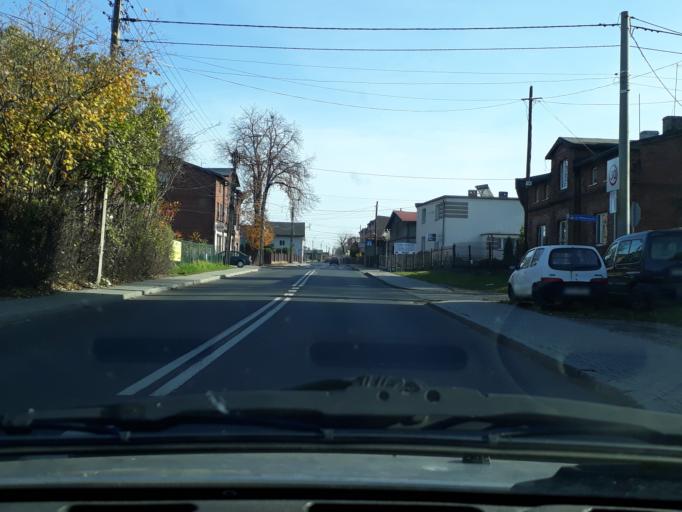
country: PL
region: Silesian Voivodeship
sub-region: Powiat tarnogorski
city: Tarnowskie Gory
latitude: 50.4220
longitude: 18.8739
